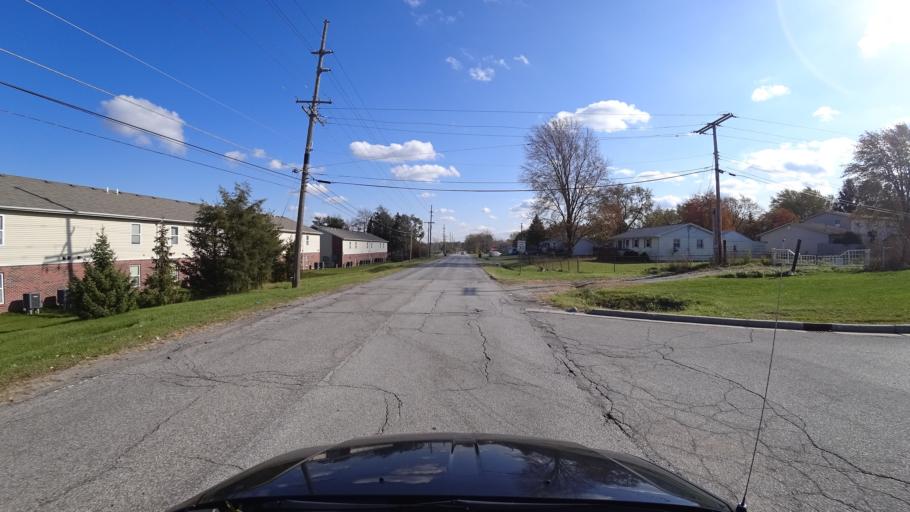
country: US
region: Indiana
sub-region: LaPorte County
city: Trail Creek
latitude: 41.6802
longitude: -86.8603
